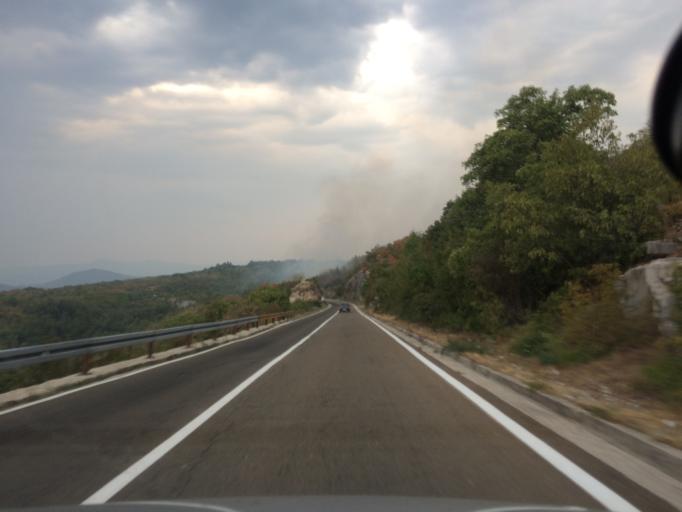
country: ME
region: Opstina Niksic
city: Niksic
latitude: 42.8694
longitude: 18.9350
